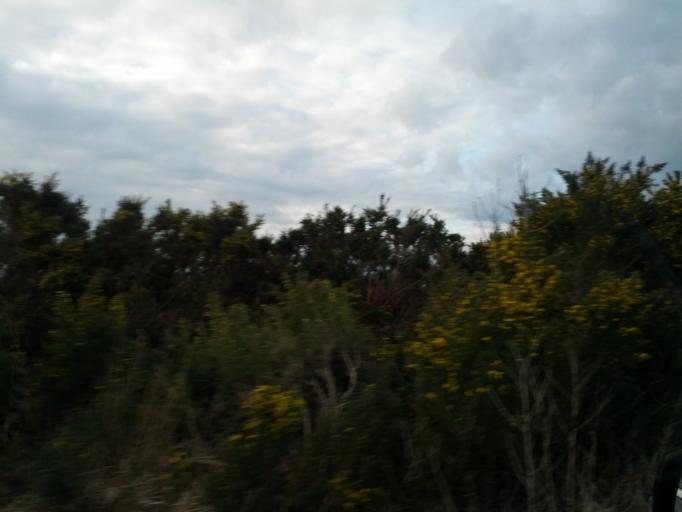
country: IE
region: Connaught
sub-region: County Galway
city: Athenry
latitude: 53.3640
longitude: -8.6653
